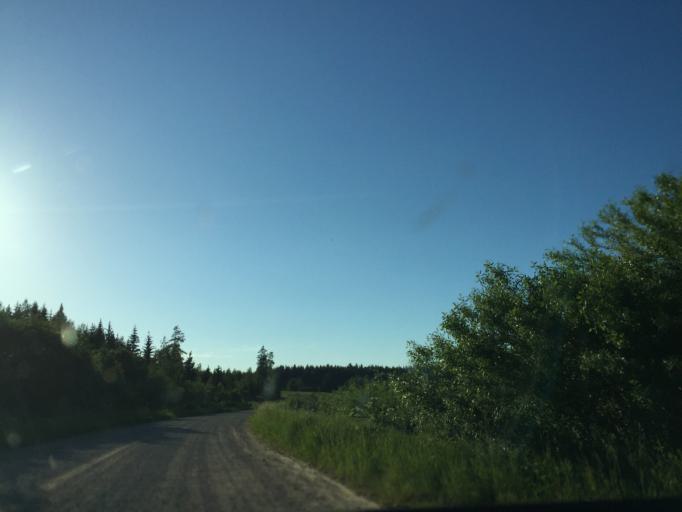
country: LV
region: Talsu Rajons
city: Sabile
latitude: 56.8601
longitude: 22.6679
